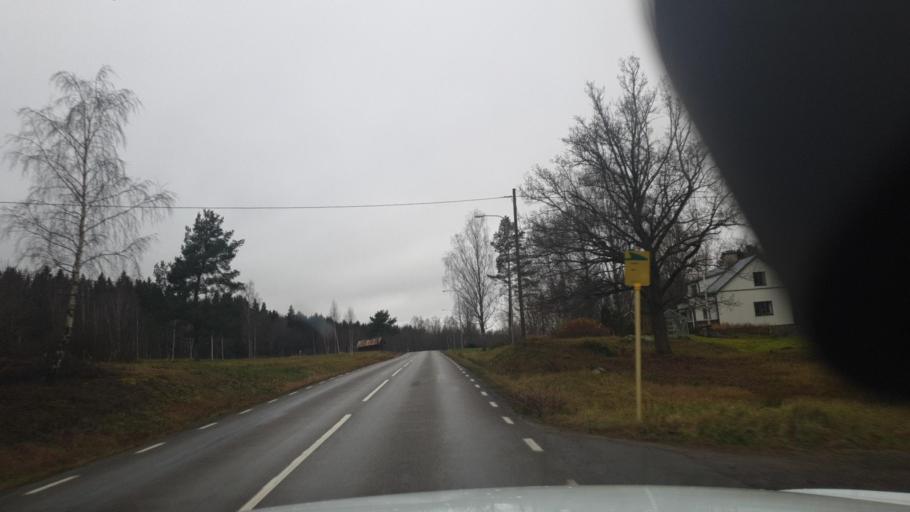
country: SE
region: Vaermland
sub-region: Arvika Kommun
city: Arvika
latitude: 59.6495
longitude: 12.4624
